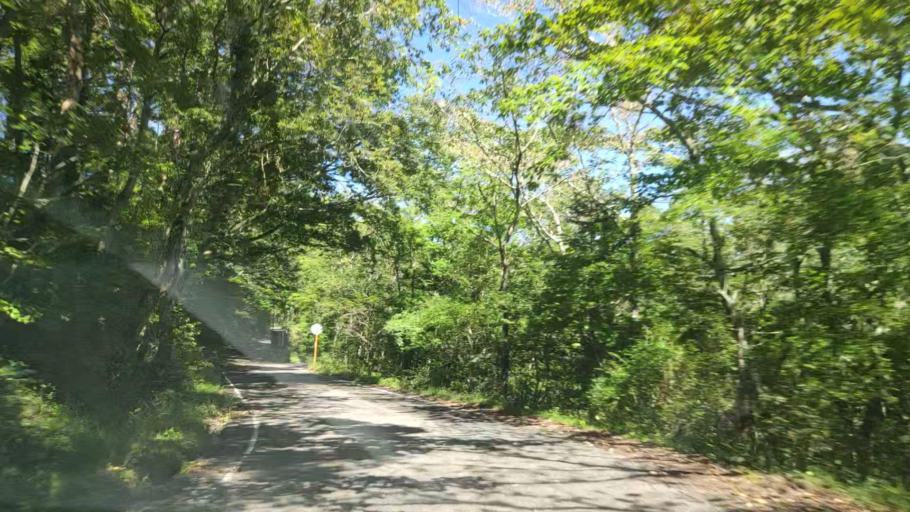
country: JP
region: Shizuoka
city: Gotemba
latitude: 35.3985
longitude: 138.8617
